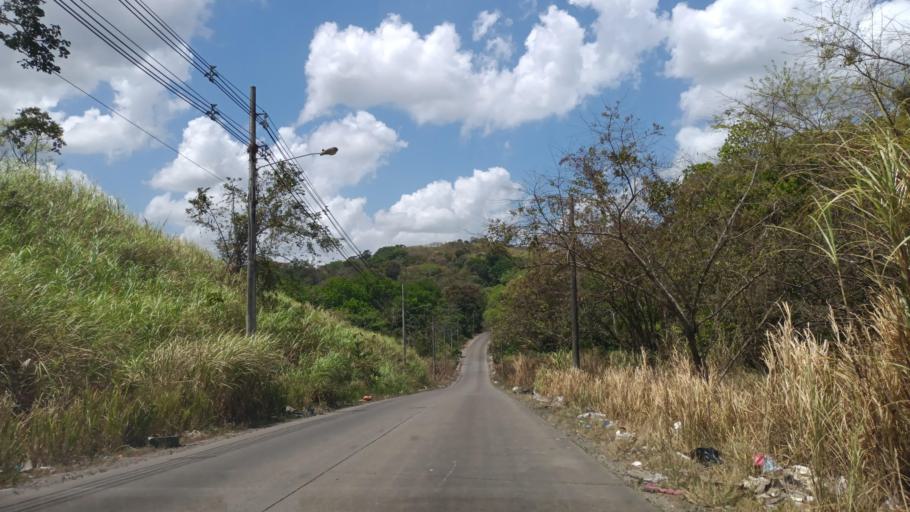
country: PA
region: Panama
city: Las Cumbres
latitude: 9.0433
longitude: -79.5581
